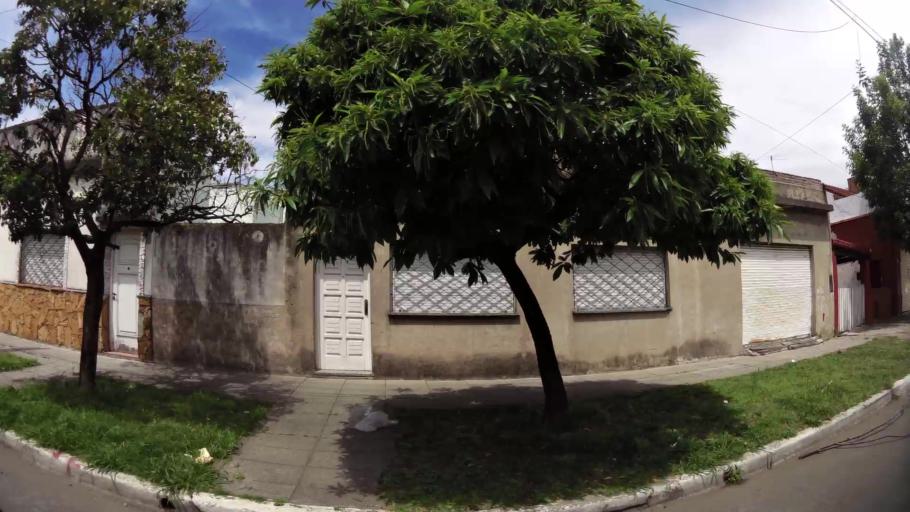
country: AR
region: Buenos Aires
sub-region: Partido de Lanus
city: Lanus
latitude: -34.6712
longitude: -58.3986
